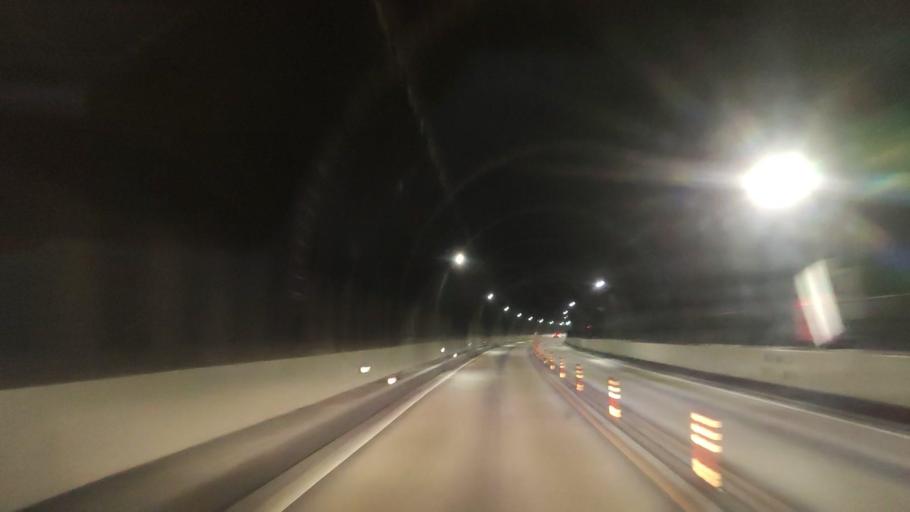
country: JP
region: Hiroshima
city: Innoshima
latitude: 34.1845
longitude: 133.0689
